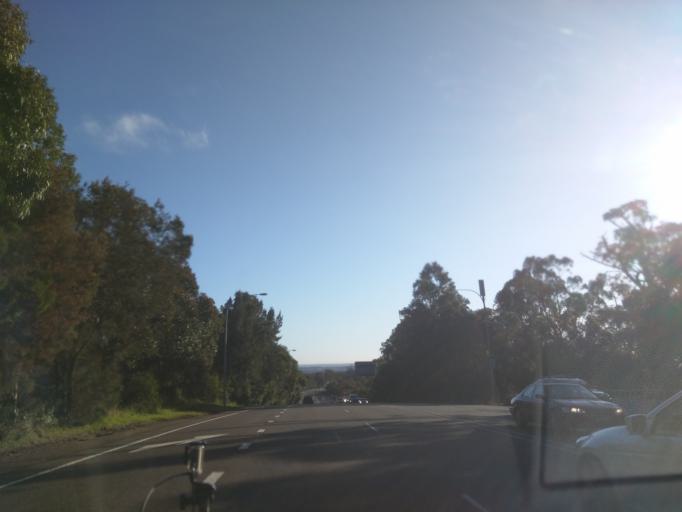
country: AU
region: New South Wales
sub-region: Hurstville
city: Lugarno
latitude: -33.9920
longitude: 151.0269
